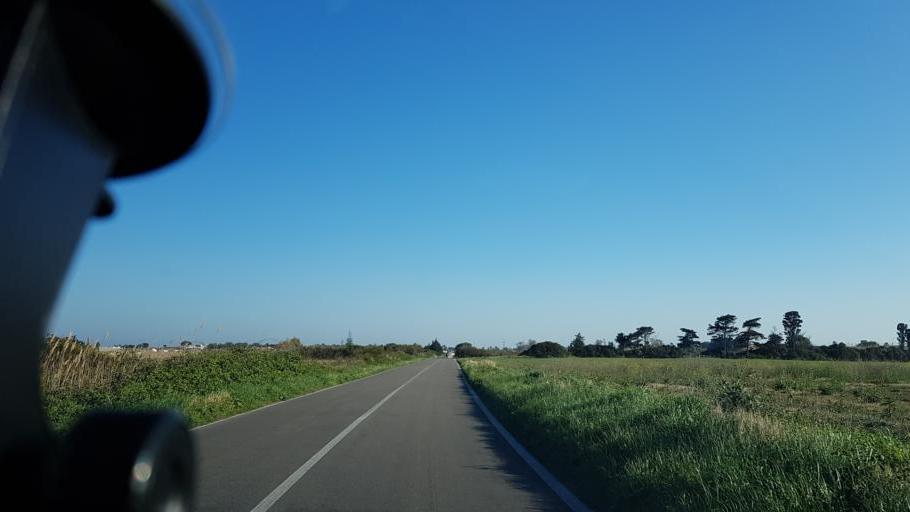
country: IT
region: Apulia
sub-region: Provincia di Lecce
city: Giorgilorio
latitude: 40.4366
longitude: 18.2390
